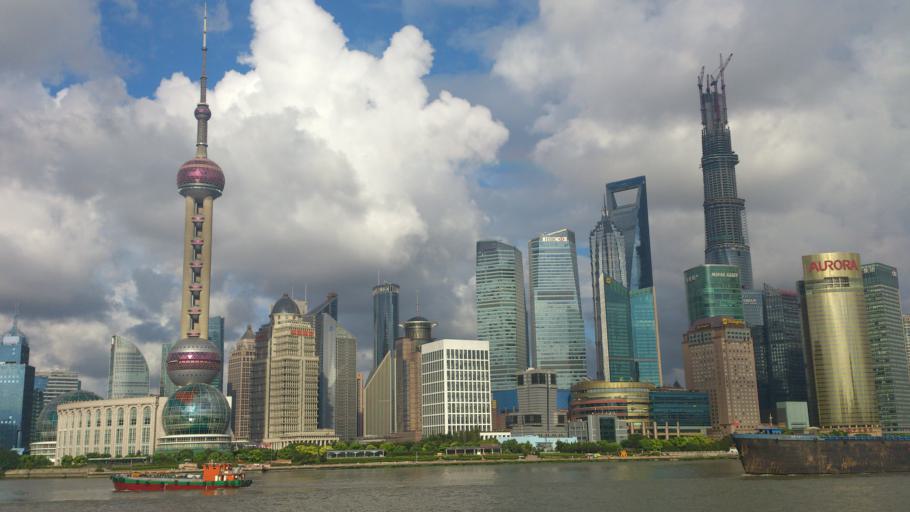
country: CN
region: Shanghai Shi
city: Hongkou
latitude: 31.2399
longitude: 121.4863
